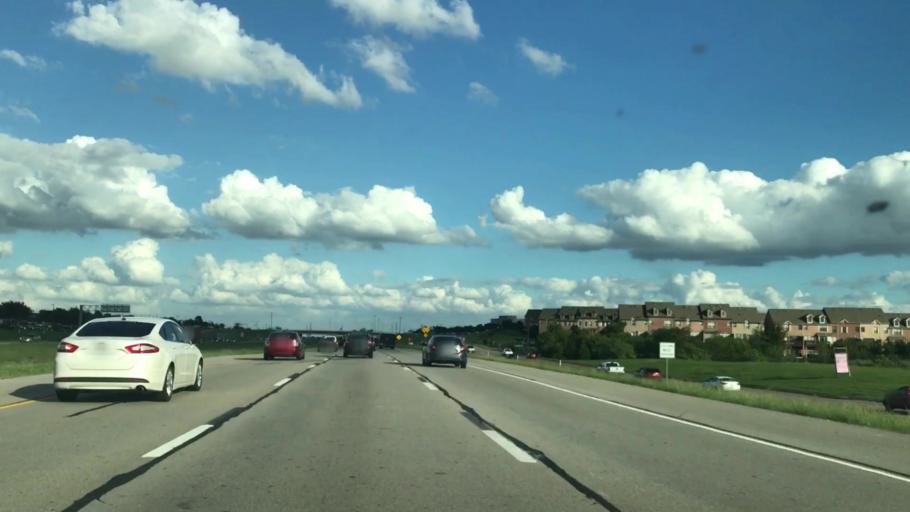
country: US
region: Texas
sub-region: Dallas County
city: Coppell
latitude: 32.9176
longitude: -96.9691
